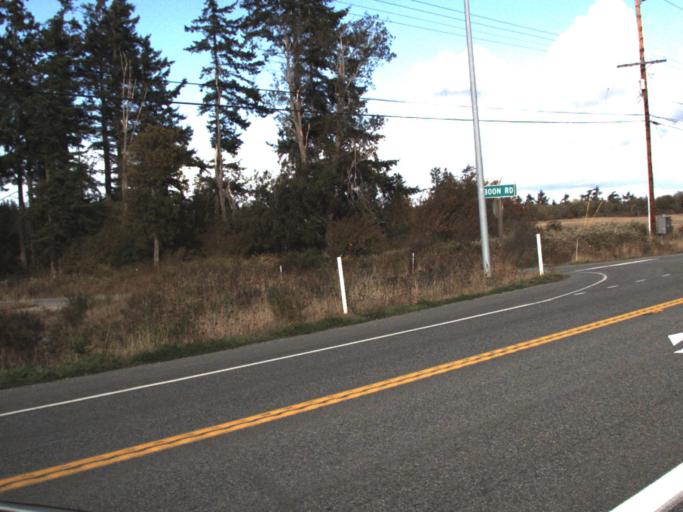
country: US
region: Washington
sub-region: Island County
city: Coupeville
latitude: 48.2606
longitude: -122.6966
